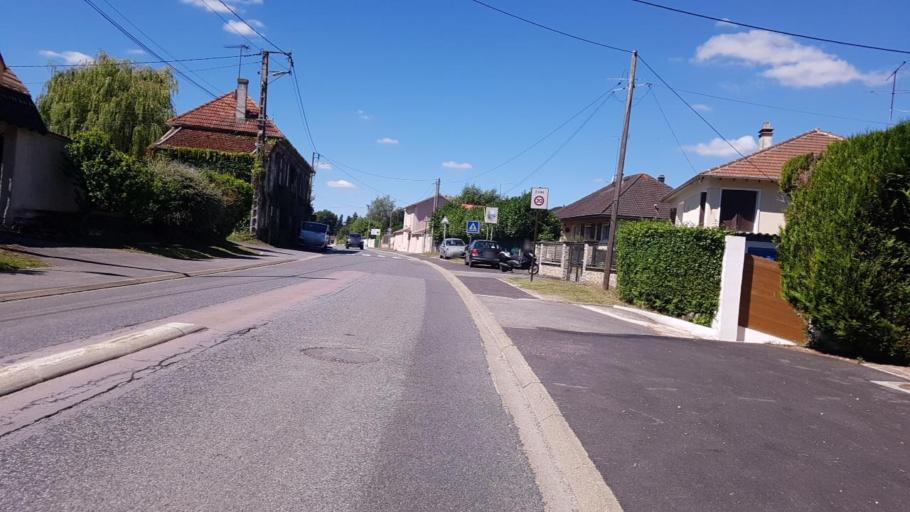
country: FR
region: Ile-de-France
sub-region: Departement de Seine-et-Marne
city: Chamigny
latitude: 48.9627
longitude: 3.1498
